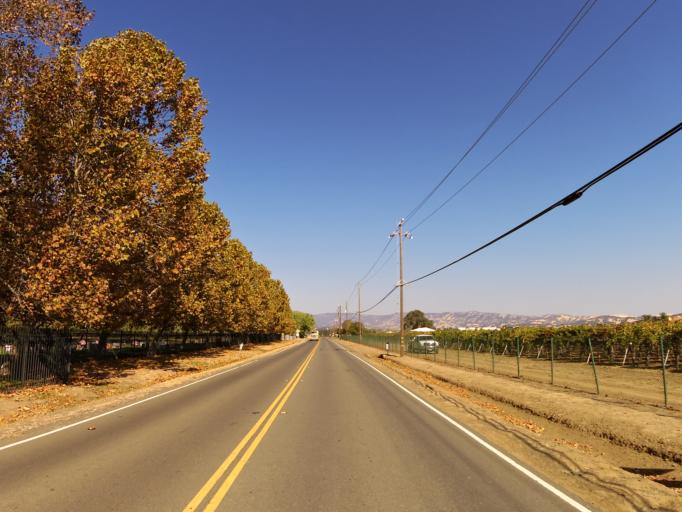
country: US
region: California
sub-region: Solano County
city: Green Valley
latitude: 38.2490
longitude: -122.1204
